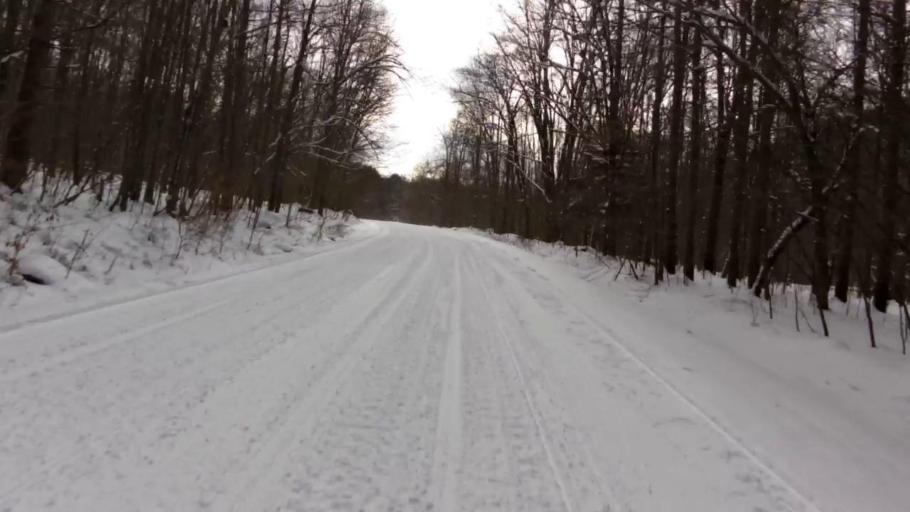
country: US
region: New York
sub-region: Cattaraugus County
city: Salamanca
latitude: 42.0867
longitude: -78.7484
